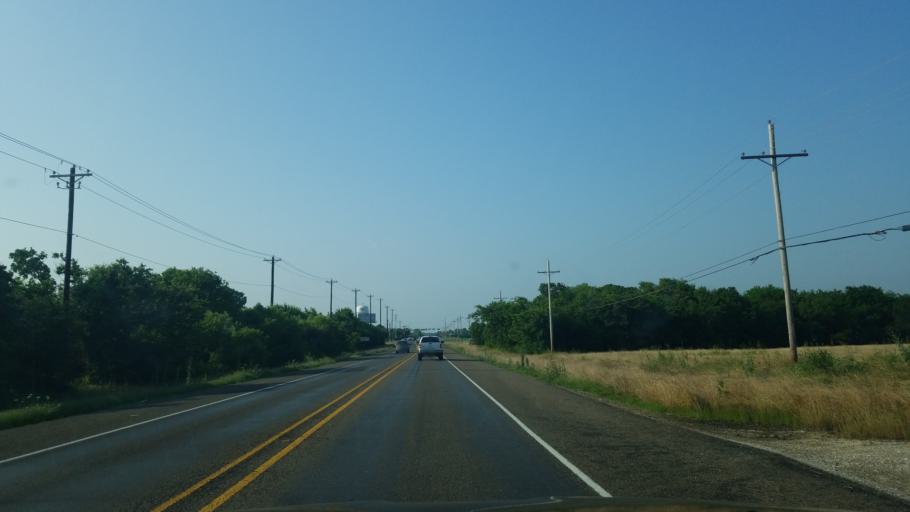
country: US
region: Texas
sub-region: Denton County
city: Pilot Point
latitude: 33.3646
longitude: -96.9649
